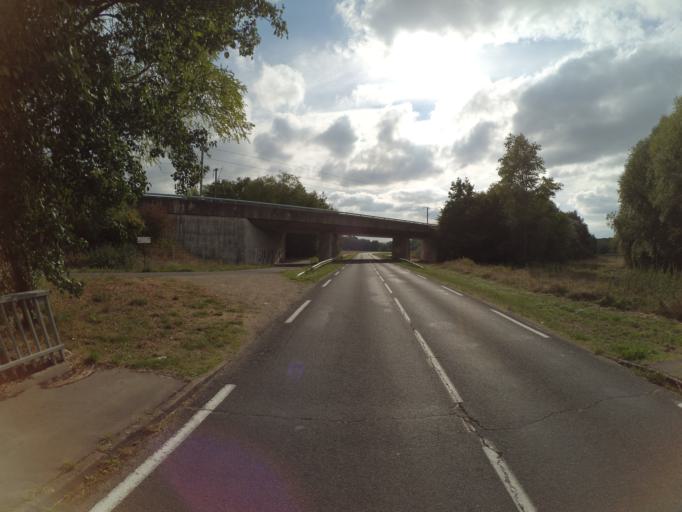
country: FR
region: Centre
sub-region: Departement d'Indre-et-Loire
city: Vernou-sur-Brenne
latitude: 47.4343
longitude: 0.8537
